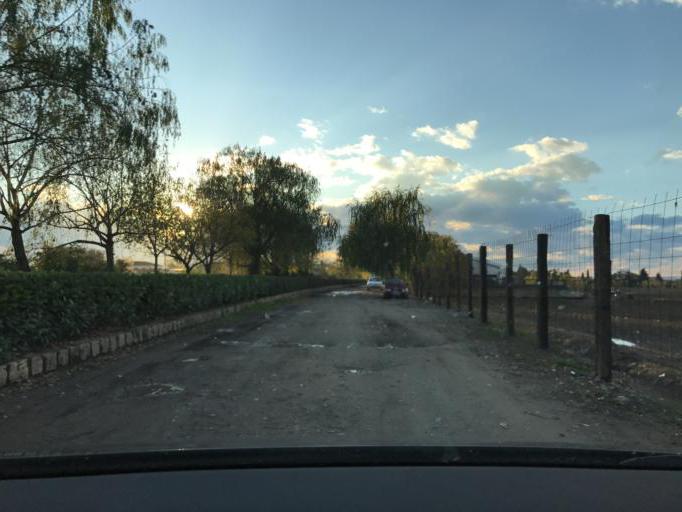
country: ES
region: Andalusia
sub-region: Provincia de Granada
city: Armilla
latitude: 37.1619
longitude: -3.6138
